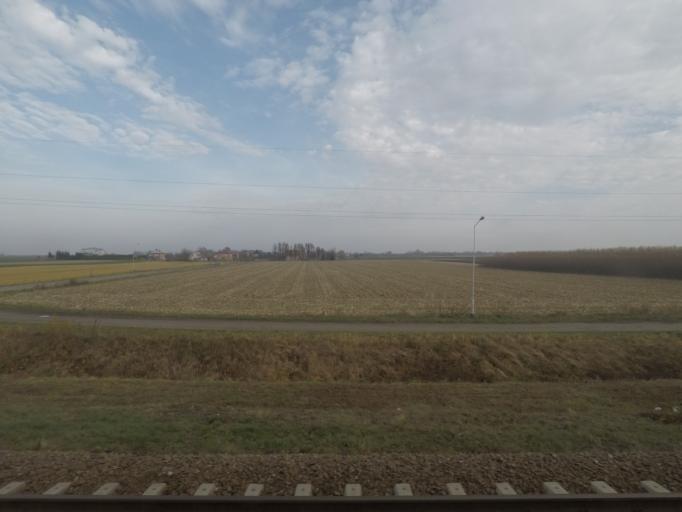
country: PL
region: Subcarpathian Voivodeship
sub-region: Powiat jaroslawski
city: Sosnica
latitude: 49.9054
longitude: 22.8498
